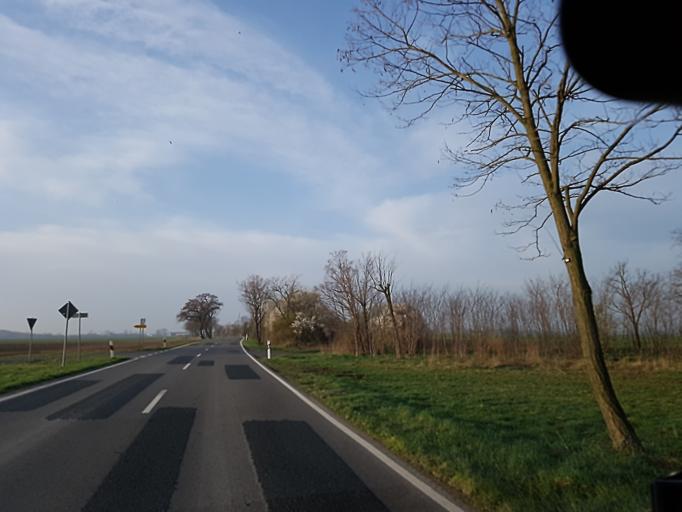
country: DE
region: Brandenburg
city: Muhlberg
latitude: 51.4363
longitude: 13.2694
